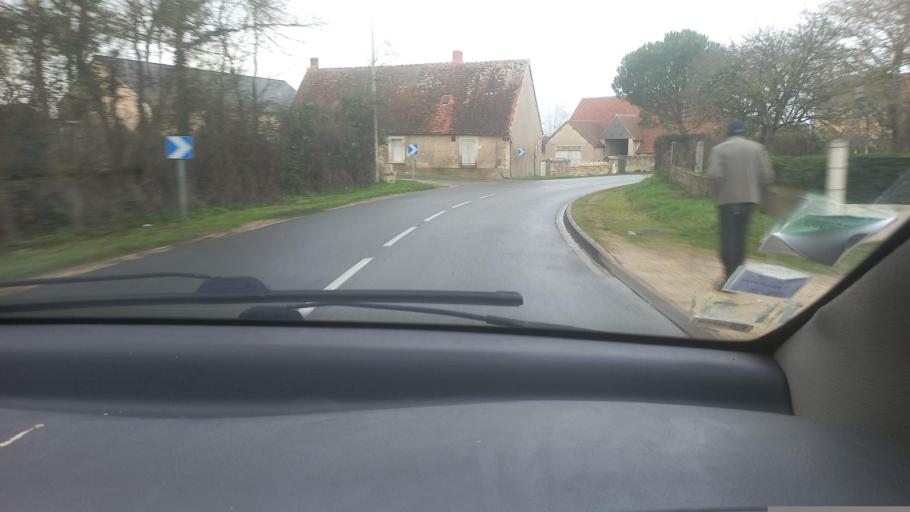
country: FR
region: Centre
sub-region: Departement de l'Indre
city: Neuvy-Pailloux
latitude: 46.7940
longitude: 1.9854
